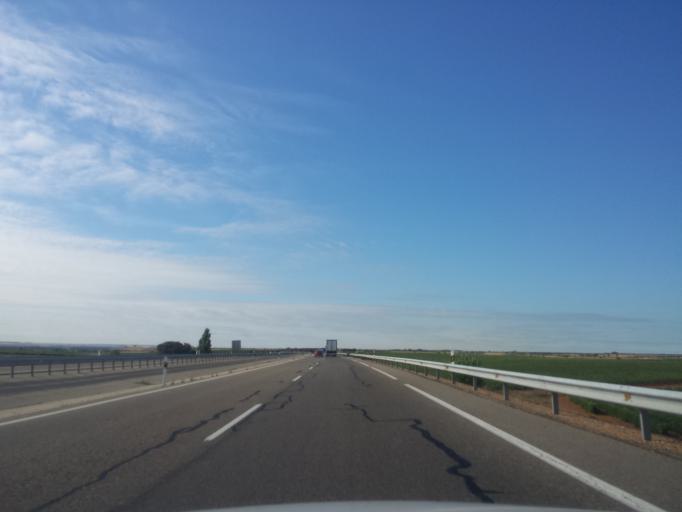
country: ES
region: Castille and Leon
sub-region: Provincia de Leon
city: Ardon
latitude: 42.4296
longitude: -5.5863
